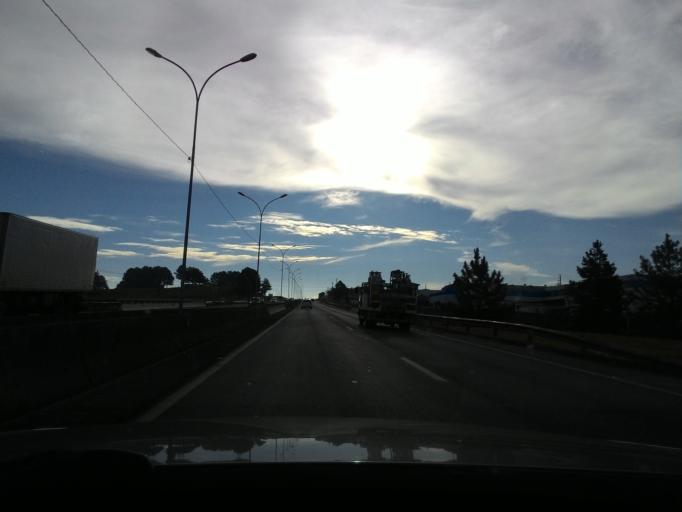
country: BR
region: Parana
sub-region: Quatro Barras
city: Quatro Barras
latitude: -25.3711
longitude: -49.1279
